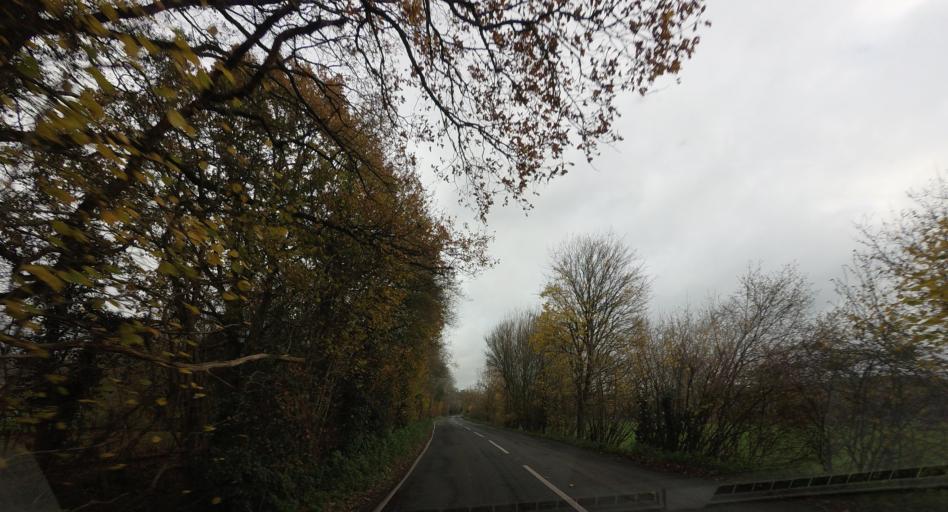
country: GB
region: England
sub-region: Kent
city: Marden
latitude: 51.1312
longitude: 0.4515
